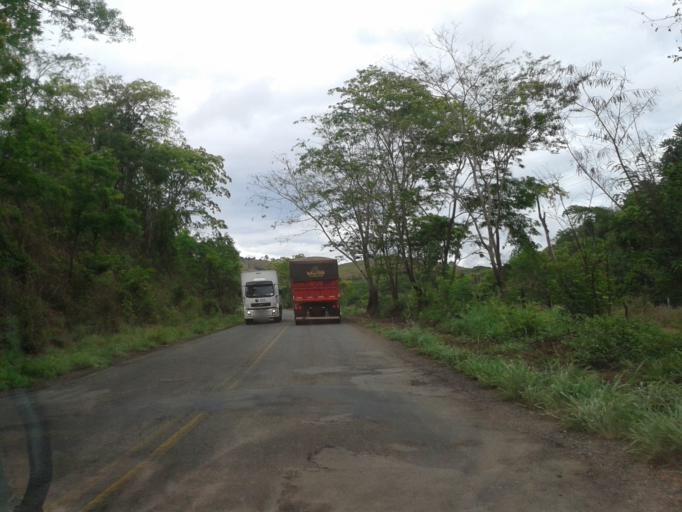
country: BR
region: Goias
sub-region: Caldas Novas
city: Caldas Novas
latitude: -18.0604
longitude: -48.6853
